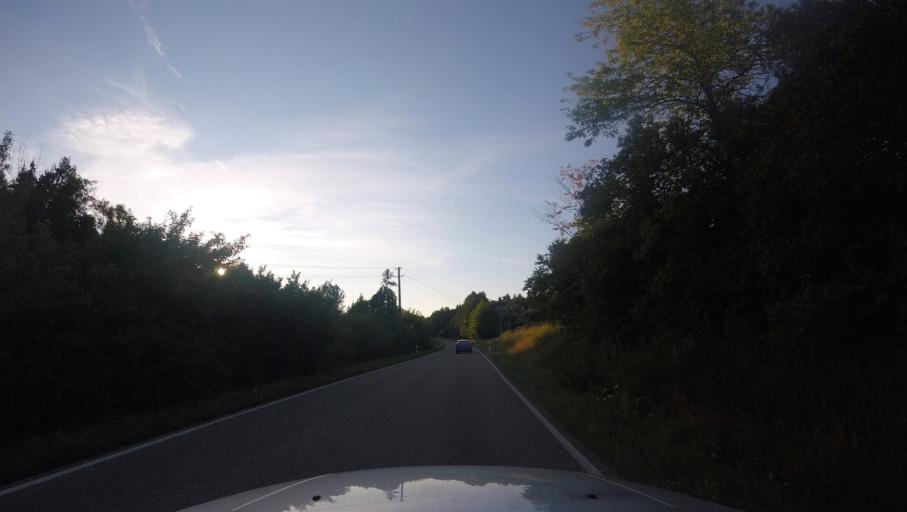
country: DE
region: Baden-Wuerttemberg
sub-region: Regierungsbezirk Stuttgart
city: Kaisersbach
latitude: 48.9249
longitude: 9.6591
